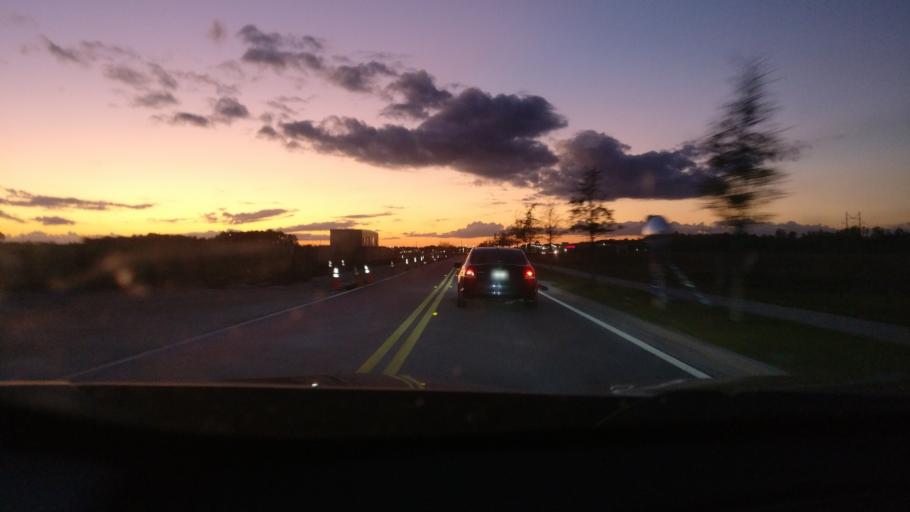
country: US
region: Florida
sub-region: Orange County
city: Hunters Creek
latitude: 28.3450
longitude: -81.4748
